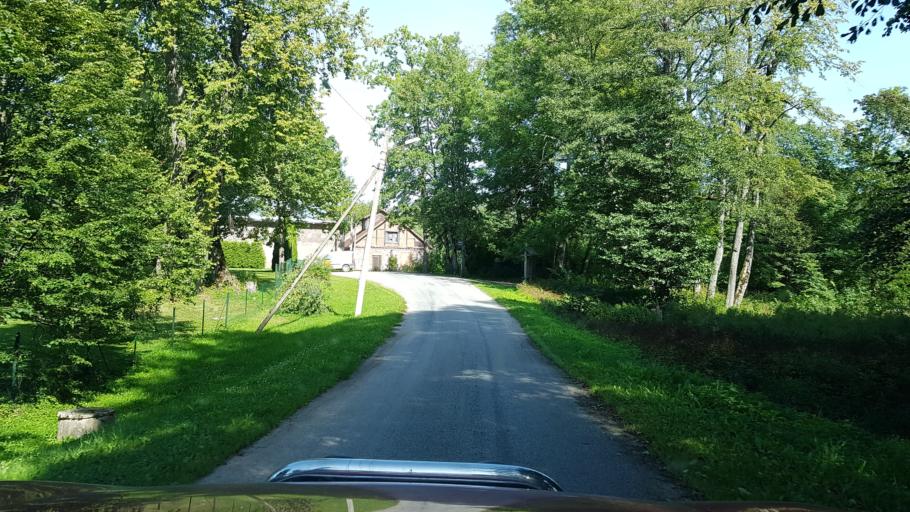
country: EE
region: Viljandimaa
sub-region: Viljandi linn
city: Viljandi
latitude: 58.4213
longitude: 25.5333
